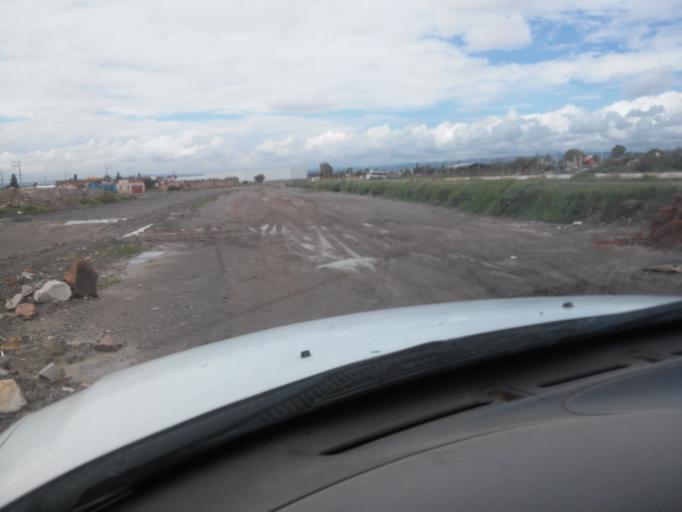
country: MX
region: Durango
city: Victoria de Durango
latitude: 24.0255
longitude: -104.6140
